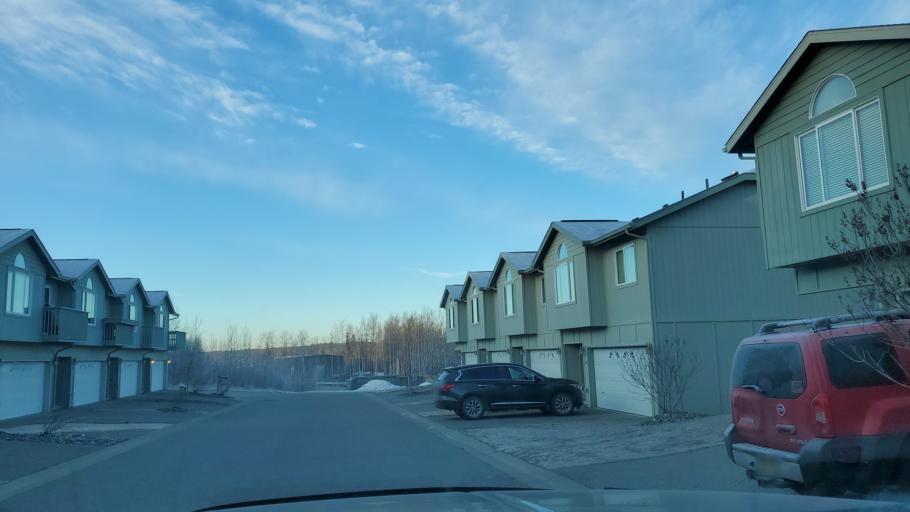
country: US
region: Alaska
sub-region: Matanuska-Susitna Borough
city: Wasilla
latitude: 61.5794
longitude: -149.4278
